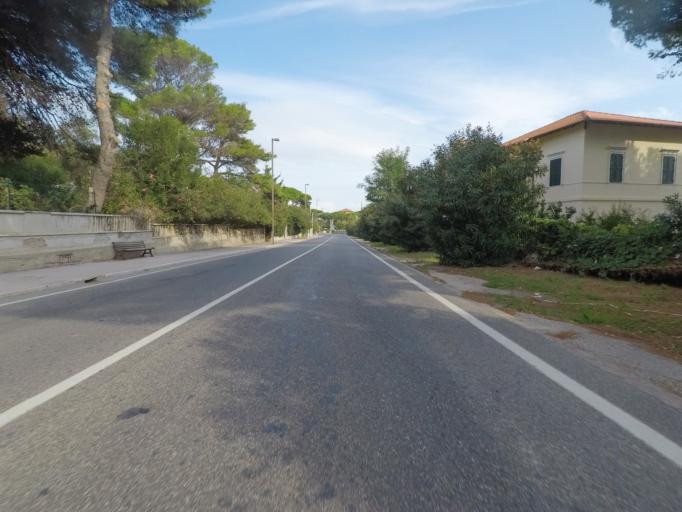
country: IT
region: Latium
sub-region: Citta metropolitana di Roma Capitale
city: Santa Marinella
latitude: 42.0322
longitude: 11.8431
